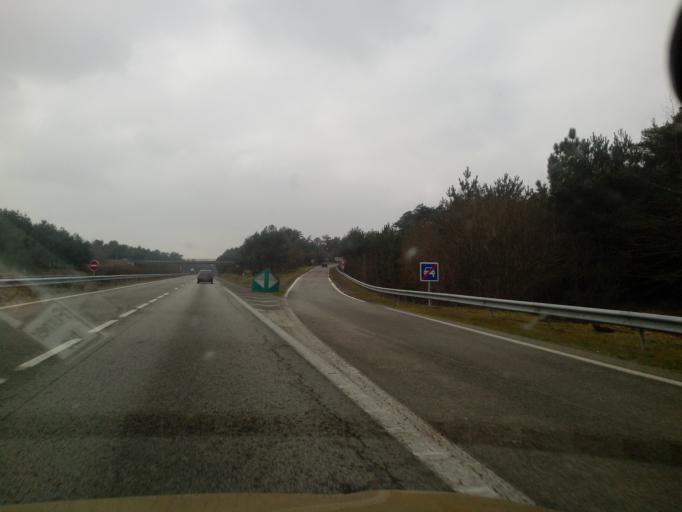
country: FR
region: Brittany
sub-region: Departement du Morbihan
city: Serent
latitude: 47.7638
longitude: -2.5128
